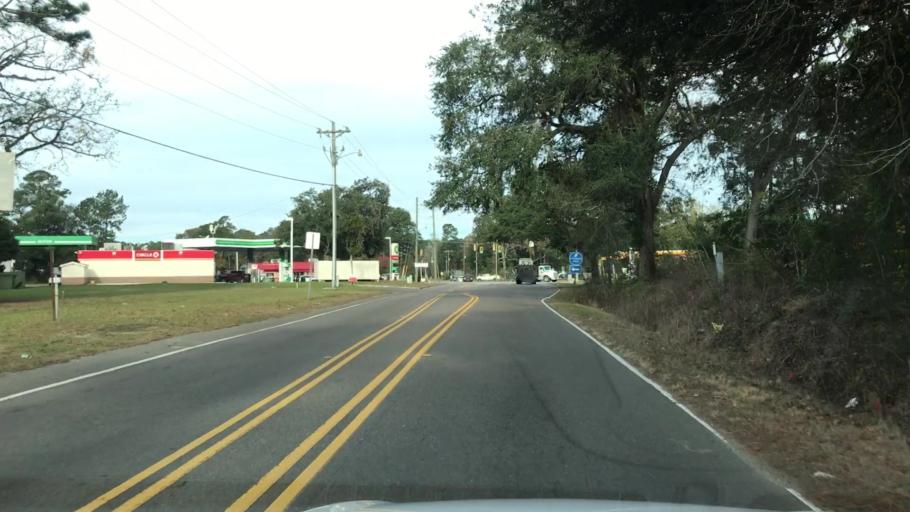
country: US
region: South Carolina
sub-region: Charleston County
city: Ravenel
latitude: 32.7753
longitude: -80.2467
